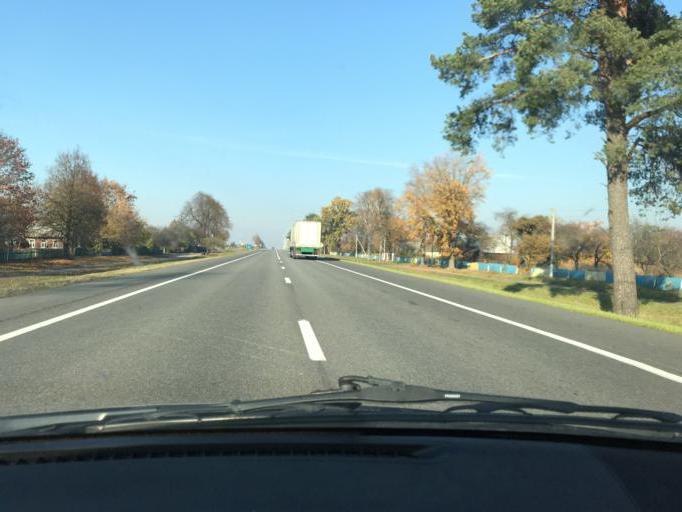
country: BY
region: Vitebsk
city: Orsha
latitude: 54.3308
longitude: 30.4465
